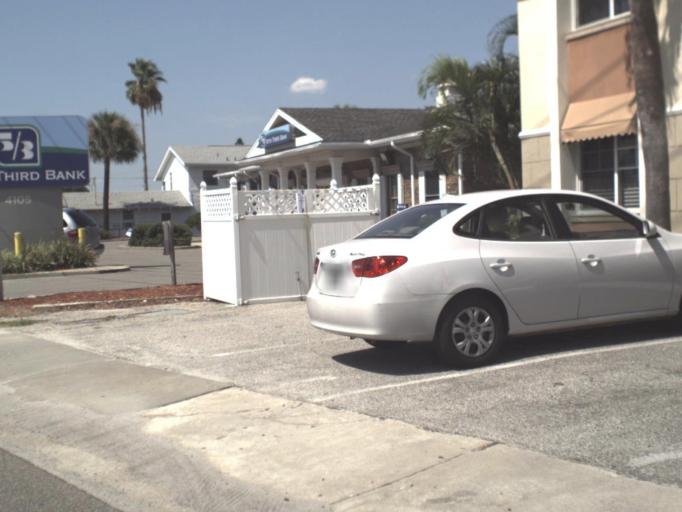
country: US
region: Florida
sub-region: Pinellas County
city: Saint Pete Beach
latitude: 27.7166
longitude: -82.7386
